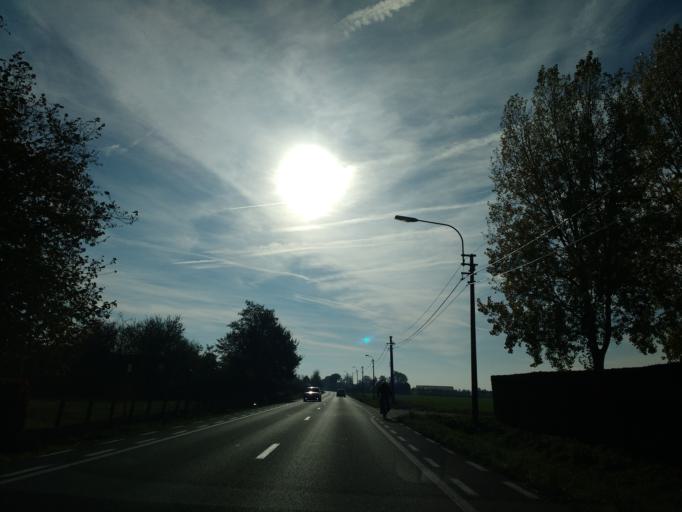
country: BE
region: Flanders
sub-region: Provincie Oost-Vlaanderen
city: Kaprijke
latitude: 51.2428
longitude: 3.6144
